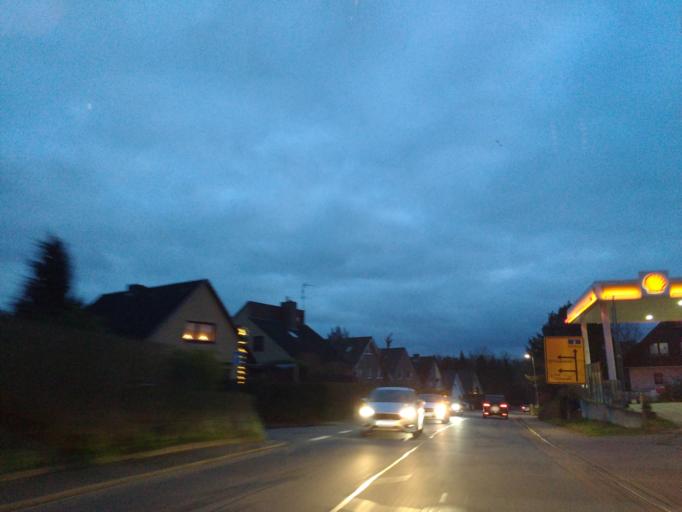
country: DE
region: Schleswig-Holstein
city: Timmendorfer Strand
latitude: 53.9948
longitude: 10.7719
